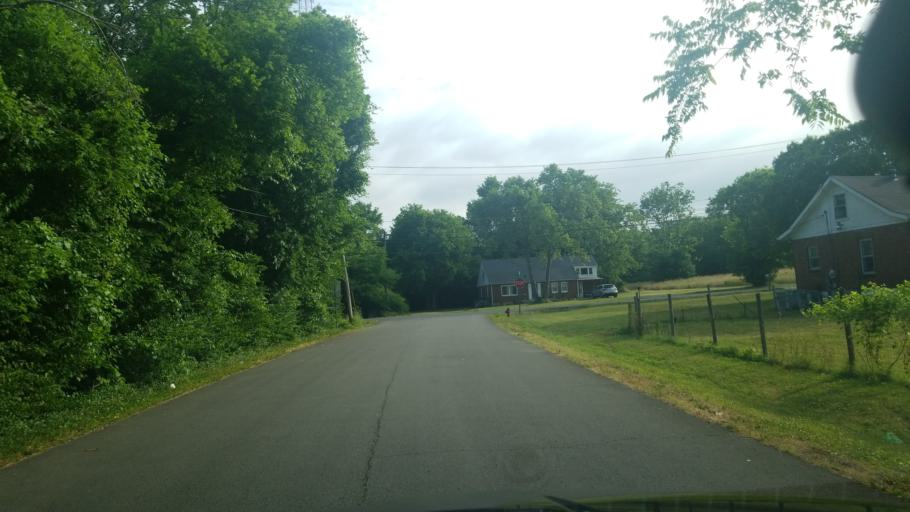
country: US
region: Tennessee
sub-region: Davidson County
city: Nashville
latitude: 36.2322
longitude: -86.7559
